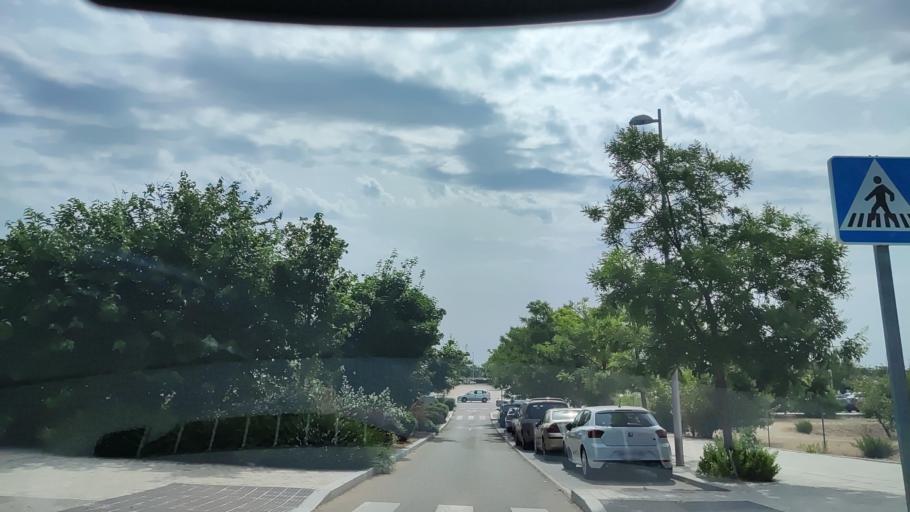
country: ES
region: Madrid
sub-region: Provincia de Madrid
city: Barajas de Madrid
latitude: 40.4860
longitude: -3.6075
